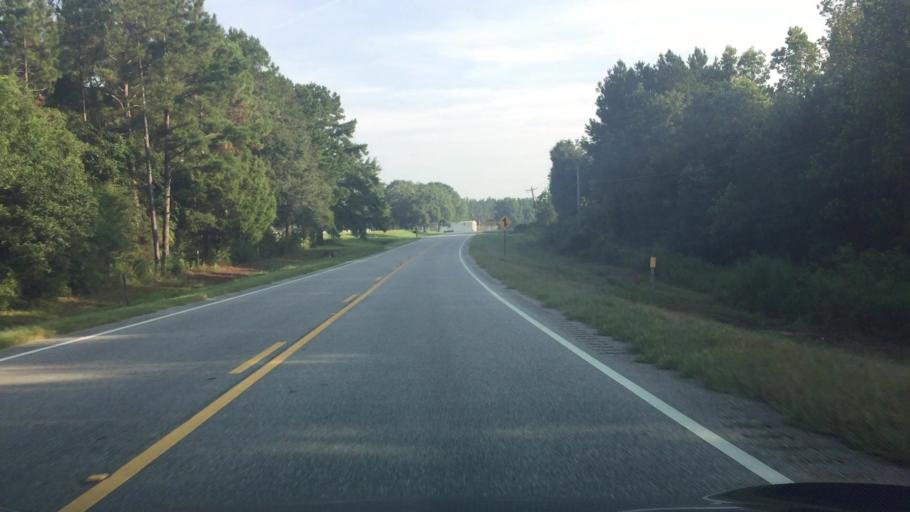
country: US
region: Alabama
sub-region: Covington County
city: Andalusia
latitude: 31.1371
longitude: -86.4597
